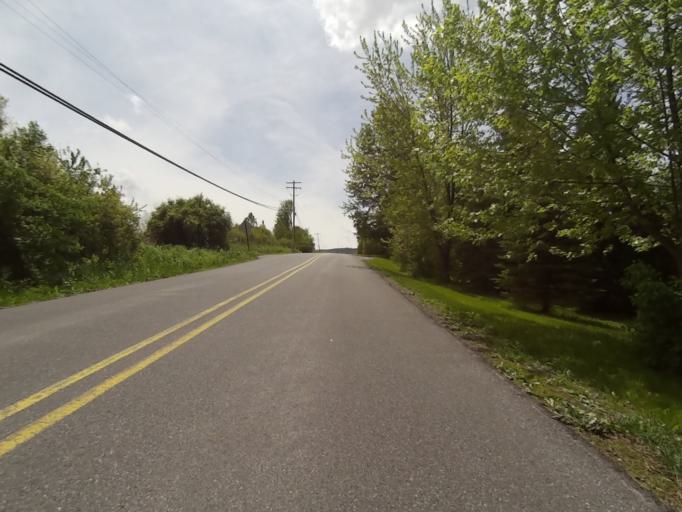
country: US
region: Pennsylvania
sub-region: Centre County
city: Boalsburg
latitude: 40.7915
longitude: -77.7584
